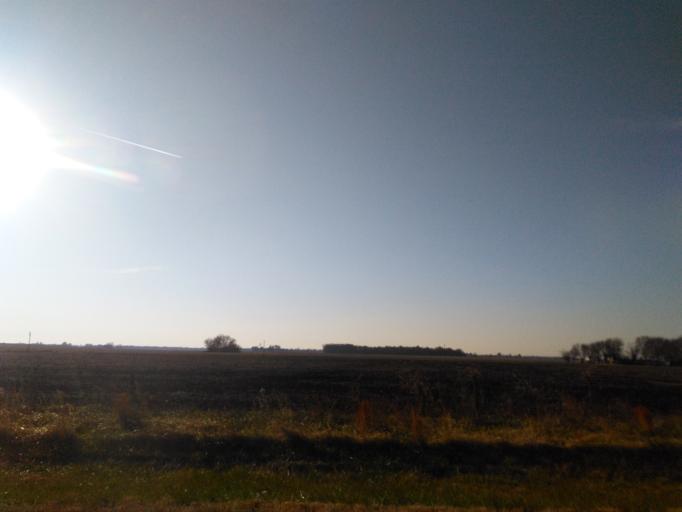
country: US
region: Illinois
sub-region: Madison County
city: Saint Jacob
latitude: 38.7622
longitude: -89.7931
